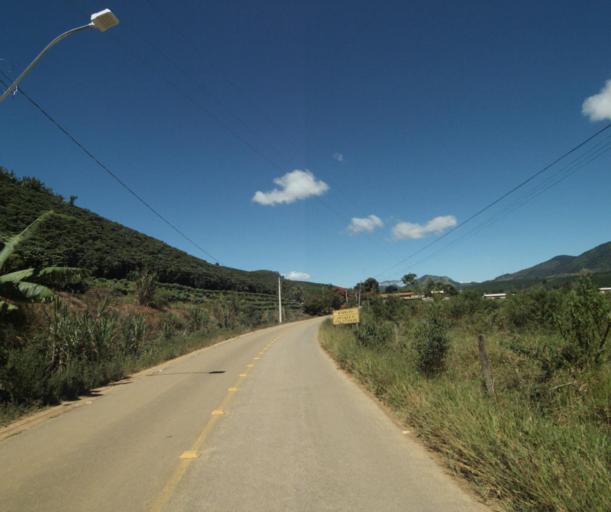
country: BR
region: Minas Gerais
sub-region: Espera Feliz
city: Espera Feliz
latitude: -20.5568
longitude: -41.8197
